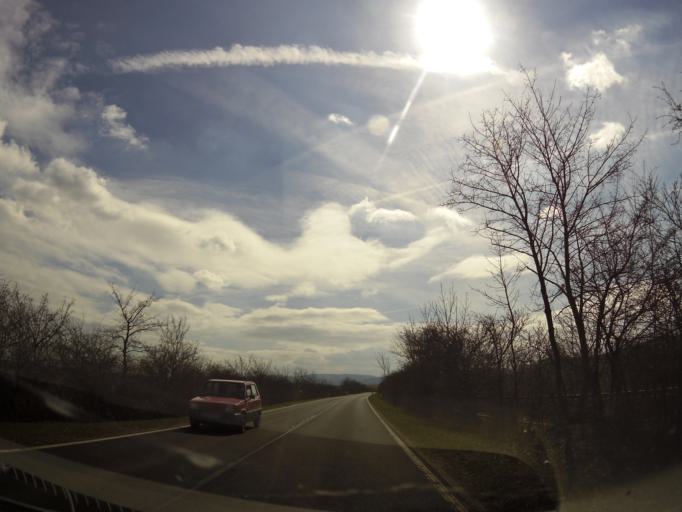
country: DE
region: Thuringia
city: Crawinkel
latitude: 50.7774
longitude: 10.7901
